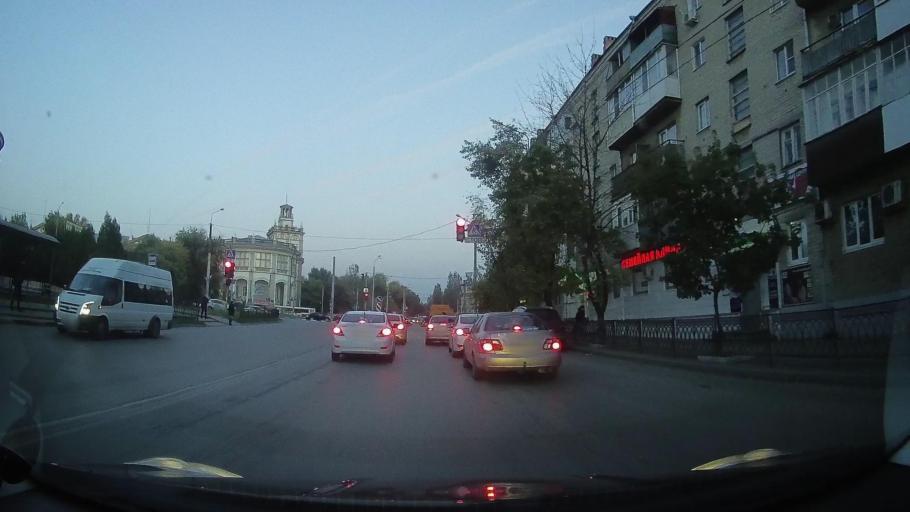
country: RU
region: Rostov
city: Rostov-na-Donu
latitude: 47.2499
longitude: 39.6958
